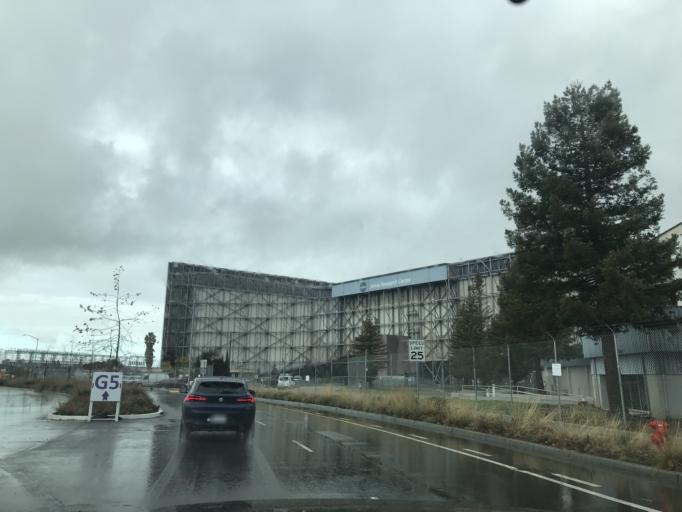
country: US
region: California
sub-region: Santa Clara County
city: Mountain View
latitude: 37.4145
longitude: -122.0640
